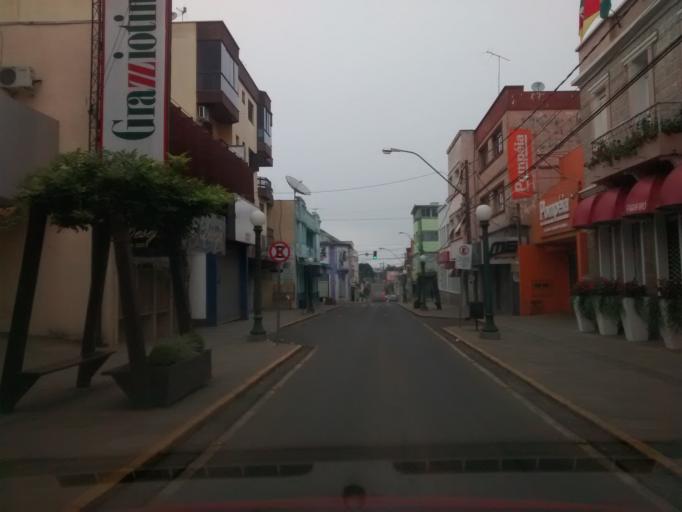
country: BR
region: Rio Grande do Sul
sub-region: Vacaria
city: Vacaria
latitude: -28.5045
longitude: -50.9382
